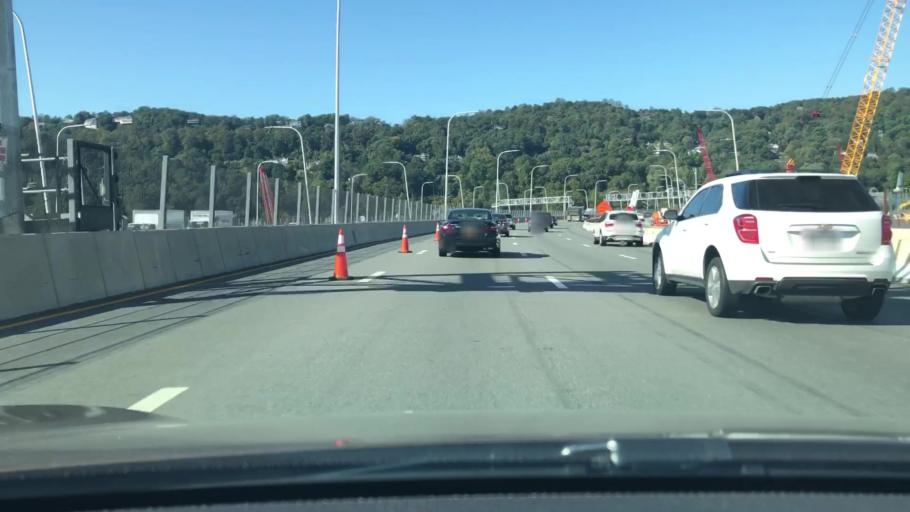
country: US
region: New York
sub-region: Rockland County
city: South Nyack
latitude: 41.0712
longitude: -73.9116
